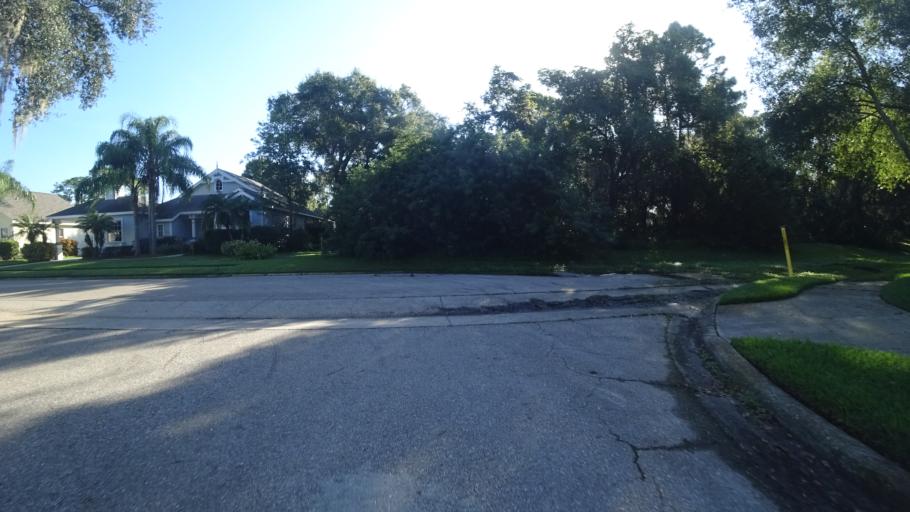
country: US
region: Florida
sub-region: Manatee County
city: Ellenton
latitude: 27.5003
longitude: -82.5026
